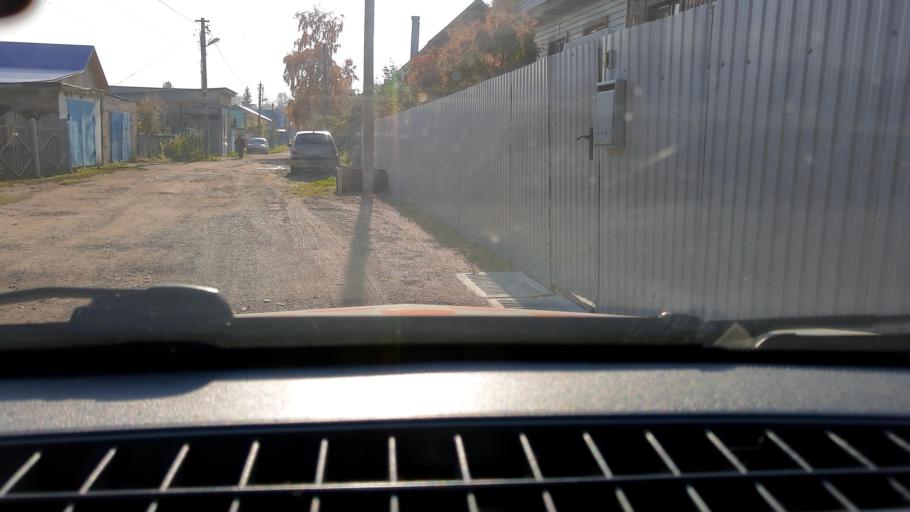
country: RU
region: Bashkortostan
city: Ufa
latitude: 54.8389
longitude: 56.1552
